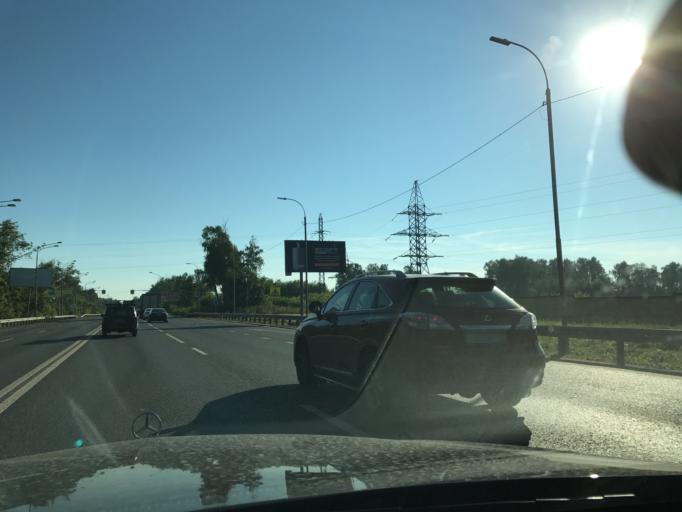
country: RU
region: Moskovskaya
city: Balashikha
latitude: 55.8455
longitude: 37.9585
